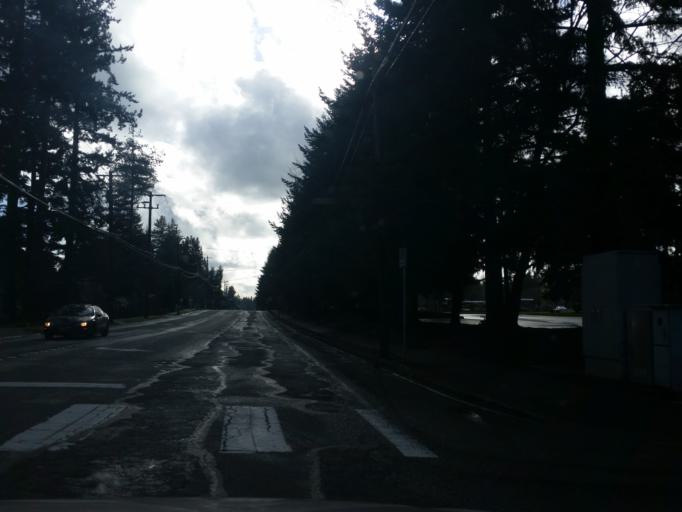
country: US
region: Washington
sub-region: Snohomish County
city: Lynnwood
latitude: 47.8178
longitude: -122.3250
